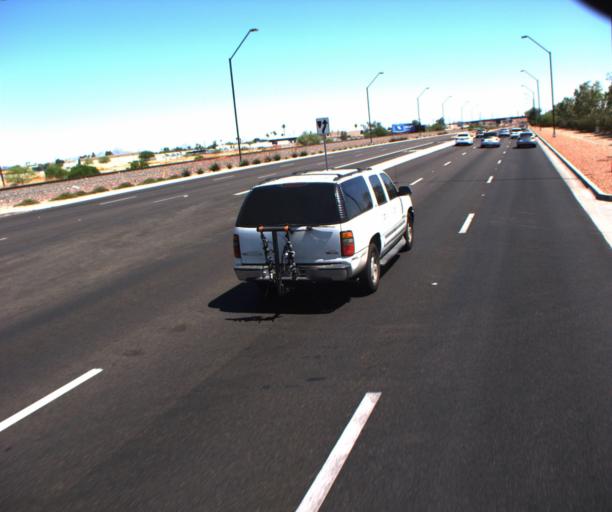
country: US
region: Arizona
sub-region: Maricopa County
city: Peoria
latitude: 33.5736
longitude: -112.2284
